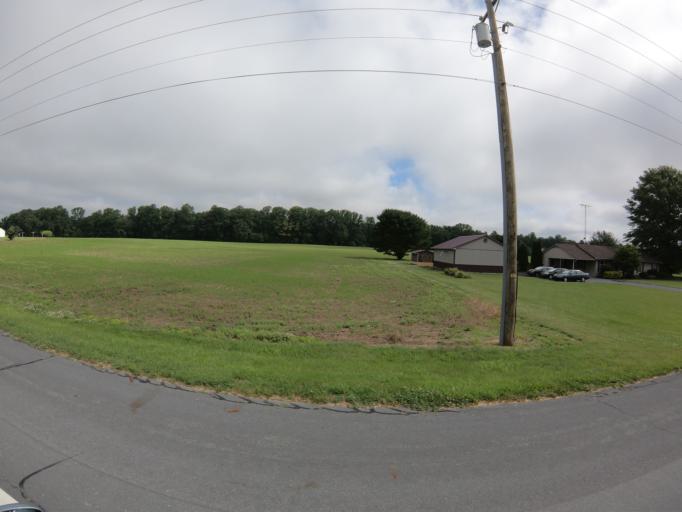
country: US
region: Delaware
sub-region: Kent County
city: Felton
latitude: 39.0062
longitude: -75.5461
